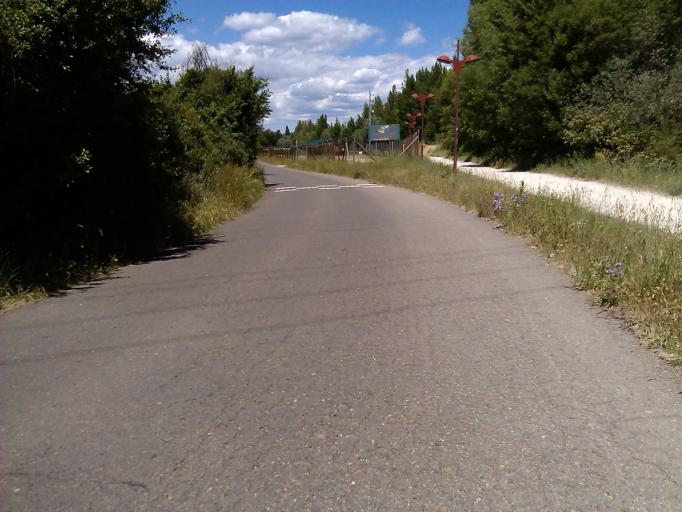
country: ES
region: Castille and Leon
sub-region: Provincia de Leon
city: Leon
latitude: 42.5865
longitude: -5.5517
